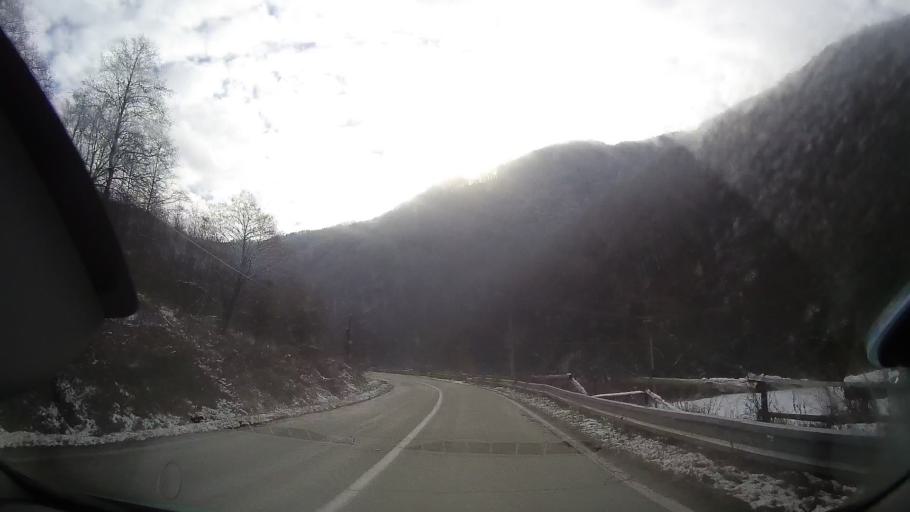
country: RO
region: Alba
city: Salciua de Sus
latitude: 46.4011
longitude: 23.3637
